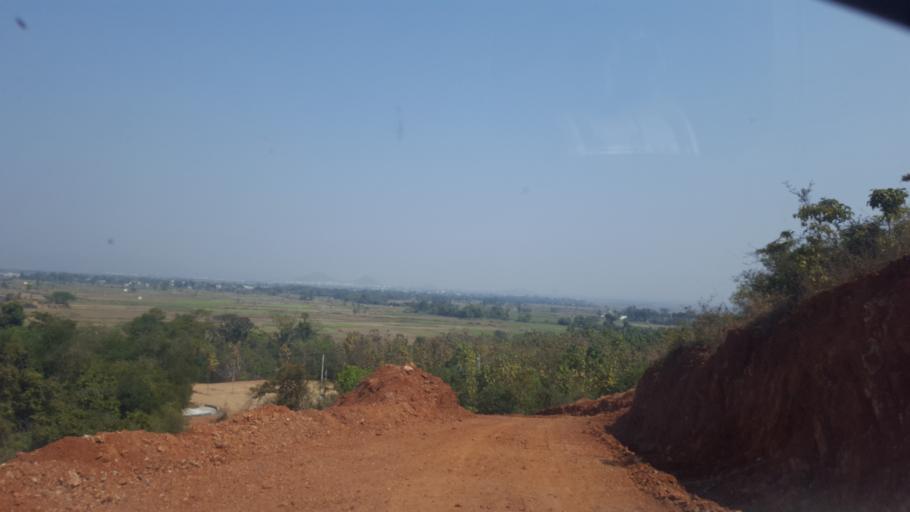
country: IN
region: Andhra Pradesh
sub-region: Srikakulam
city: Palasa
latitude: 18.7208
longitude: 84.3951
